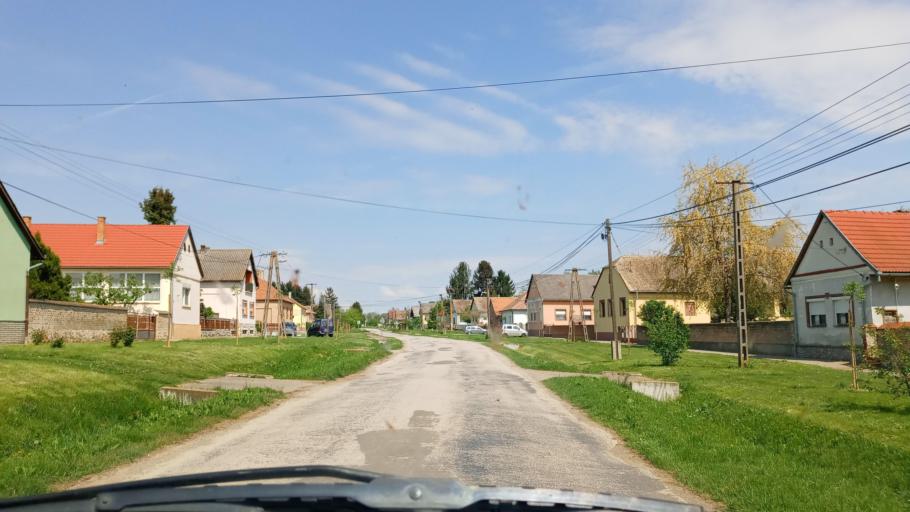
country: HR
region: Osjecko-Baranjska
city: Beli Manastir
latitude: 45.8665
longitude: 18.5855
